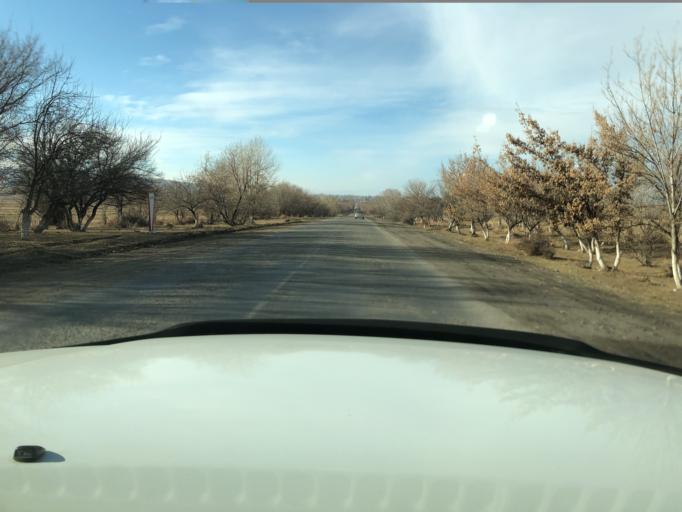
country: KG
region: Ysyk-Koel
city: Pokrovka
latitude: 42.3307
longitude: 77.9703
